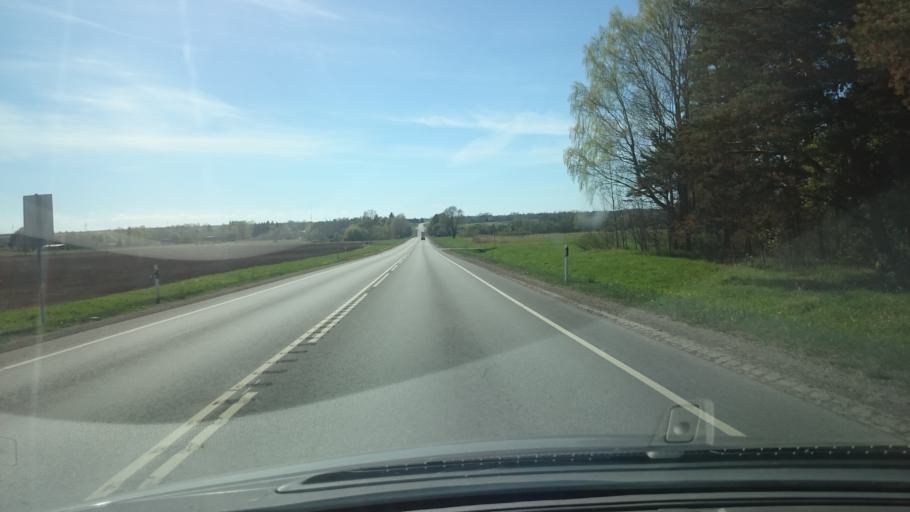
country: EE
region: Ida-Virumaa
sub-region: Puessi linn
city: Pussi
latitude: 59.4121
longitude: 27.0216
